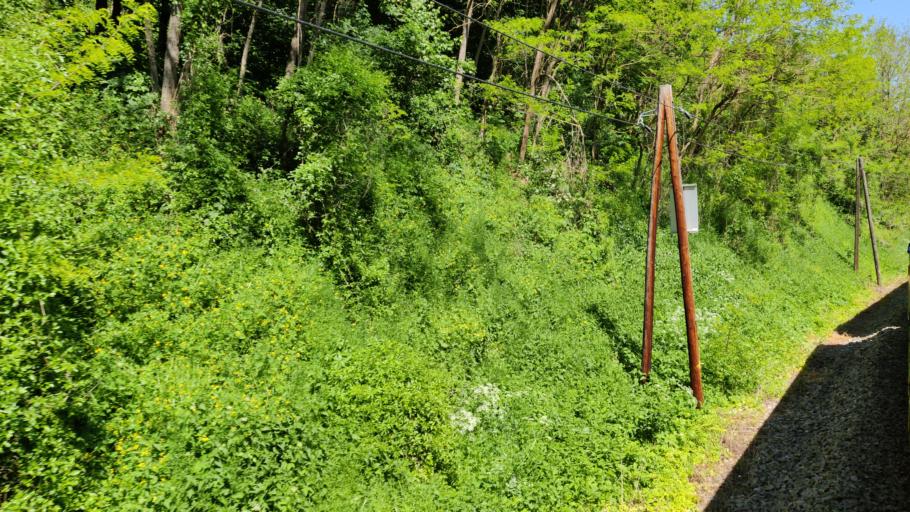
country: AT
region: Lower Austria
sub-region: Politischer Bezirk Horn
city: Gars am Kamp
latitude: 48.6228
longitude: 15.6431
